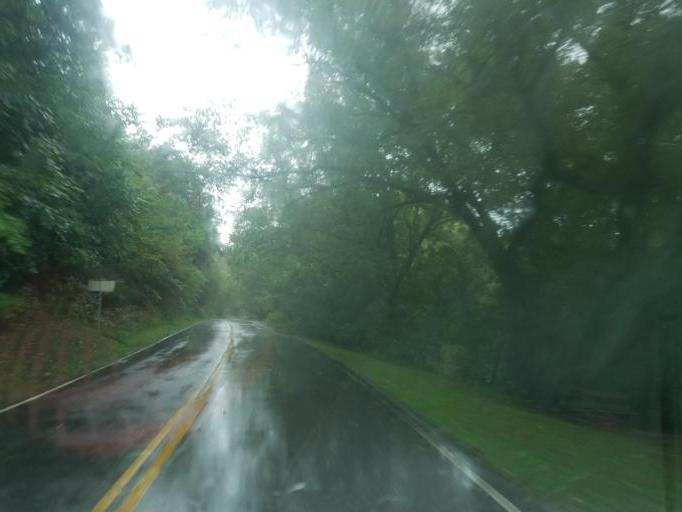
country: US
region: Kentucky
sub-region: Greenup County
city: Greenup
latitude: 38.5020
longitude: -82.9699
